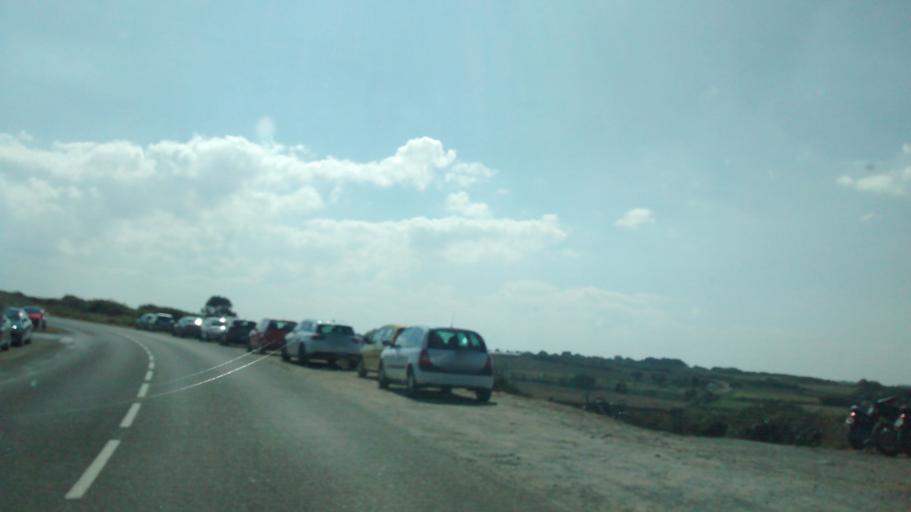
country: FR
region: Brittany
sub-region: Departement d'Ille-et-Vilaine
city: Cancale
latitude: 48.7007
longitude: -1.8599
